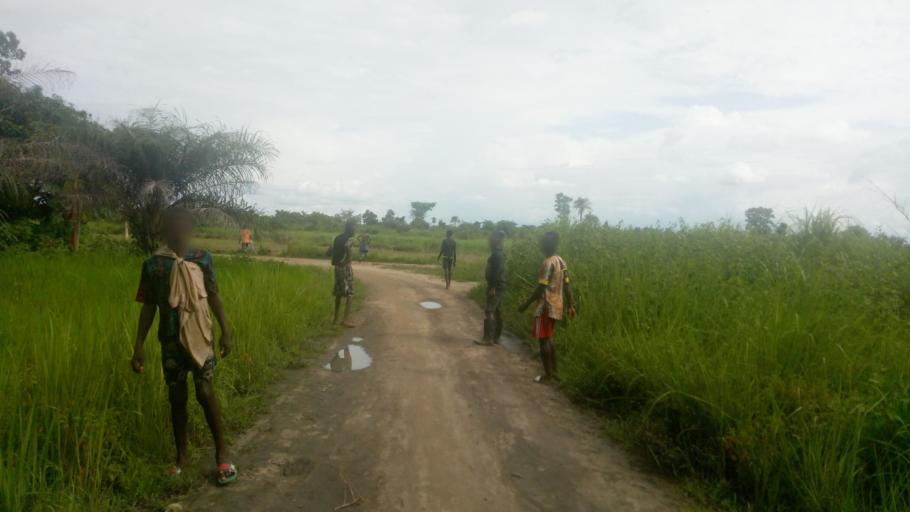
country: SL
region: Northern Province
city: Magburaka
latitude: 8.6737
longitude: -12.0323
